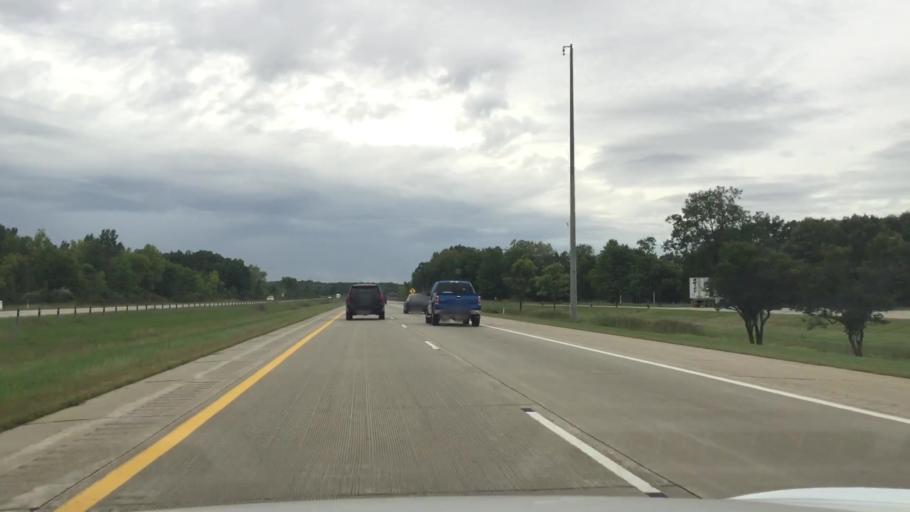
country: US
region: Michigan
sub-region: Macomb County
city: New Baltimore
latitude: 42.7430
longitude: -82.7189
